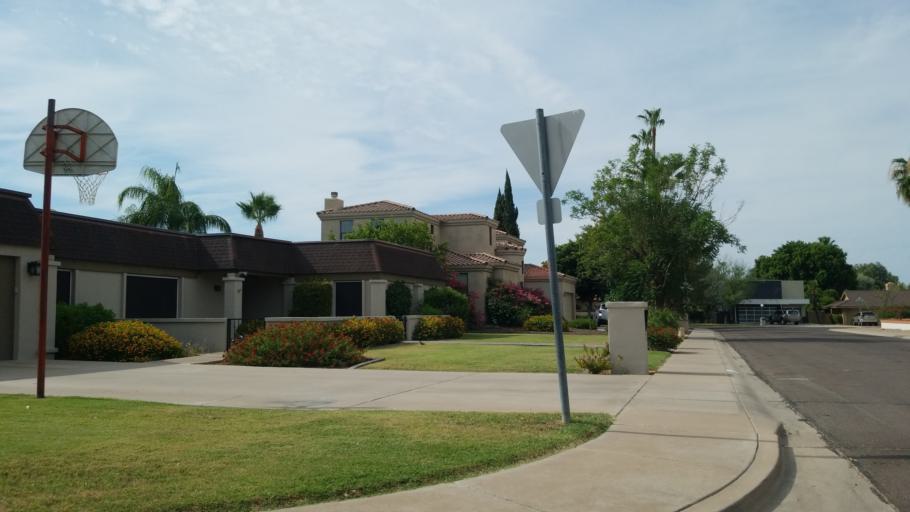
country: US
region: Arizona
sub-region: Maricopa County
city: Phoenix
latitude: 33.5603
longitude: -112.0755
